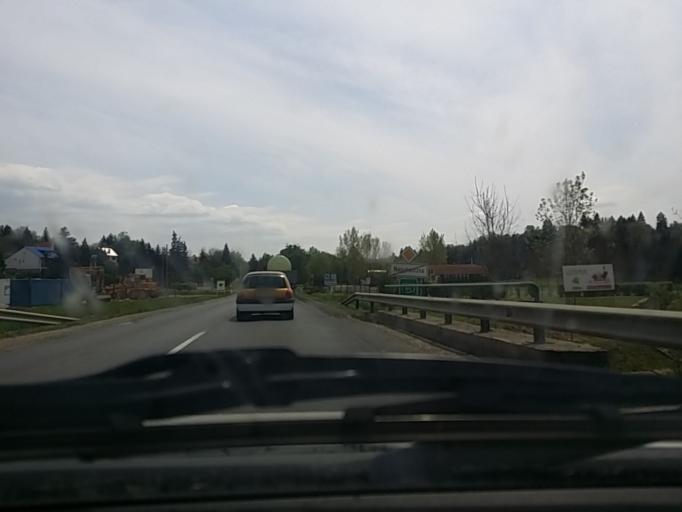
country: HU
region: Zala
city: Nagykanizsa
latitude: 46.4429
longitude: 17.0320
